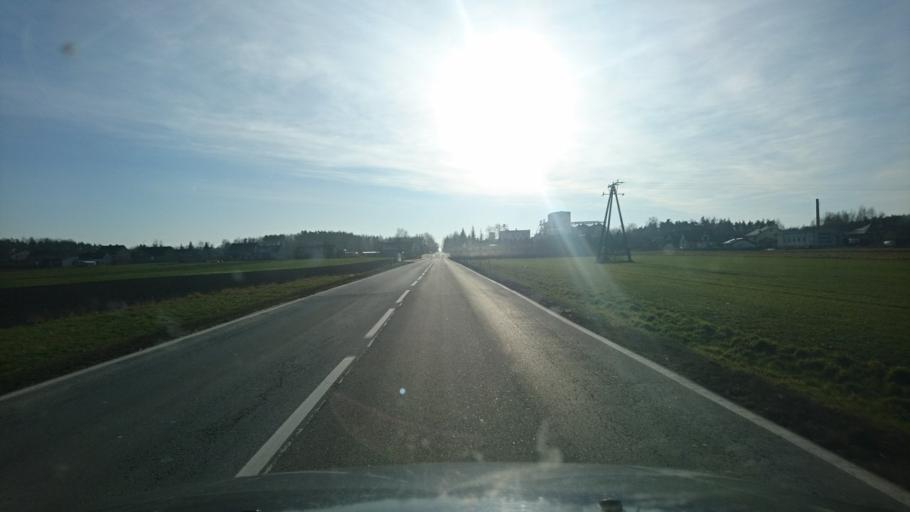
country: PL
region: Opole Voivodeship
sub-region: Powiat oleski
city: Dalachow
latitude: 51.0783
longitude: 18.6033
